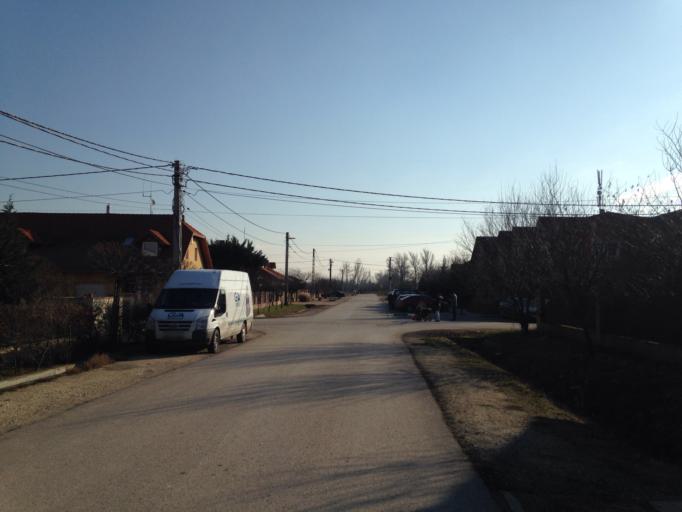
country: HU
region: Pest
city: Dunaharaszti
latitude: 47.3430
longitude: 19.0989
